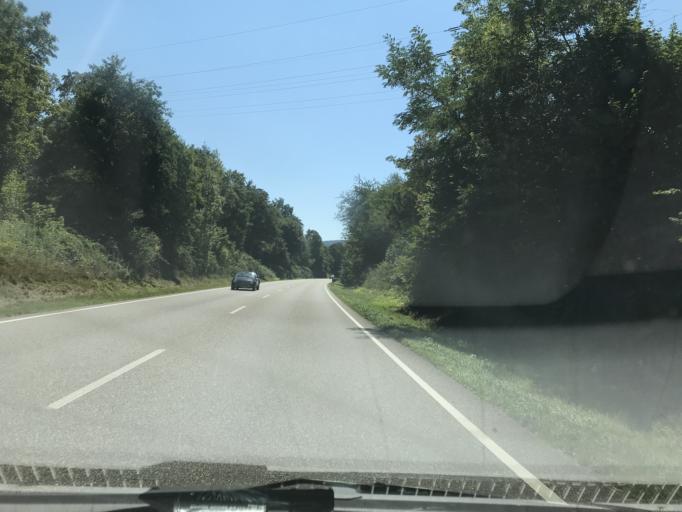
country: CH
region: Aargau
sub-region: Bezirk Rheinfelden
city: Mumpf
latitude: 47.5636
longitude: 7.9244
